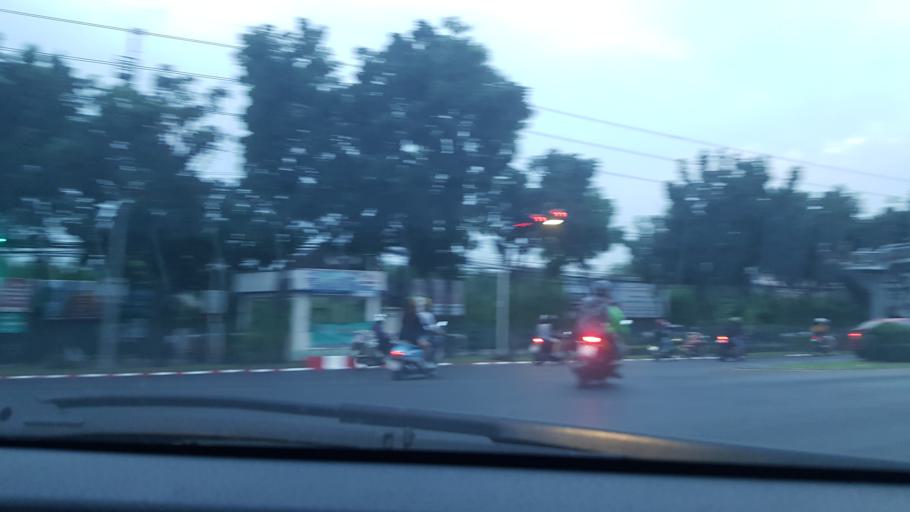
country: TH
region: Bangkok
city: Nong Khaem
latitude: 13.7074
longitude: 100.3641
